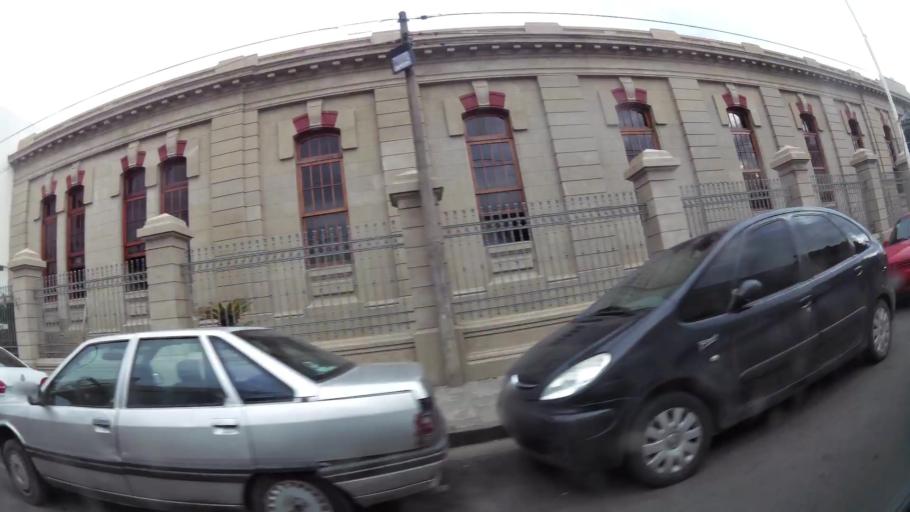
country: AR
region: Buenos Aires
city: San Nicolas de los Arroyos
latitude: -33.3348
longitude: -60.2231
